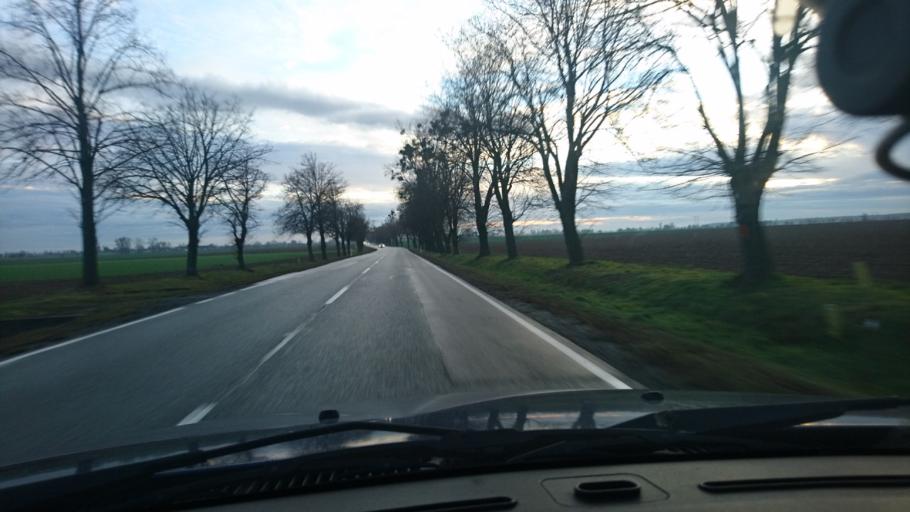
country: PL
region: Opole Voivodeship
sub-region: Powiat kluczborski
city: Byczyna
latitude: 51.0436
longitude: 18.1956
